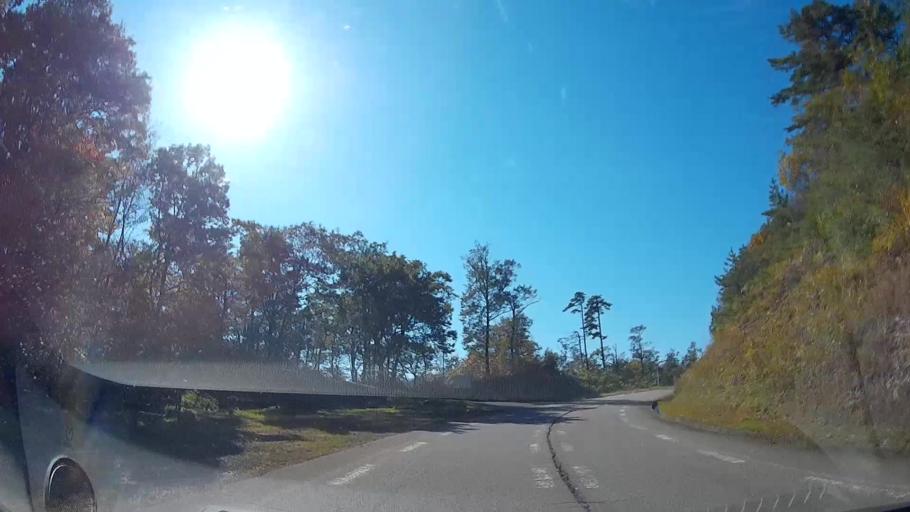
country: JP
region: Toyama
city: Fukumitsu
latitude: 36.5165
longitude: 136.8324
